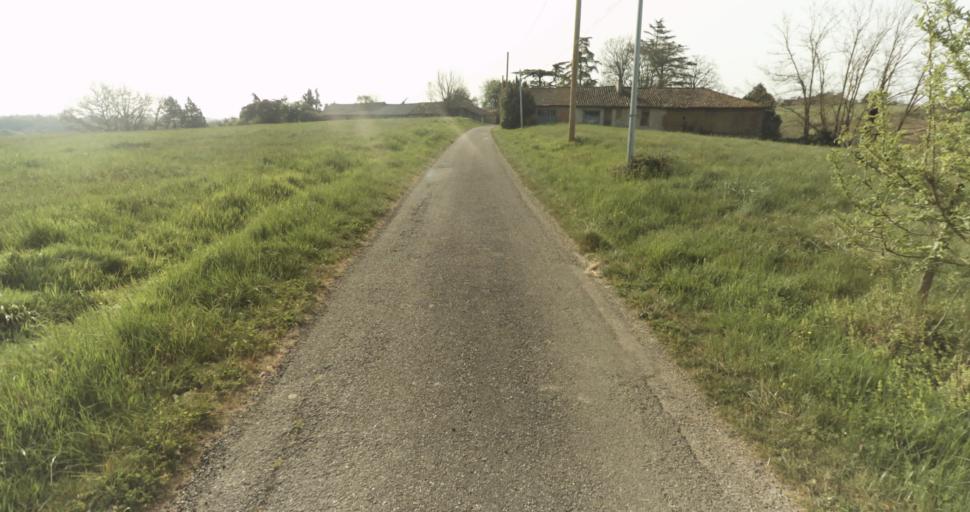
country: FR
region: Midi-Pyrenees
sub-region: Departement du Tarn-et-Garonne
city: Moissac
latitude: 44.1541
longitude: 1.0435
